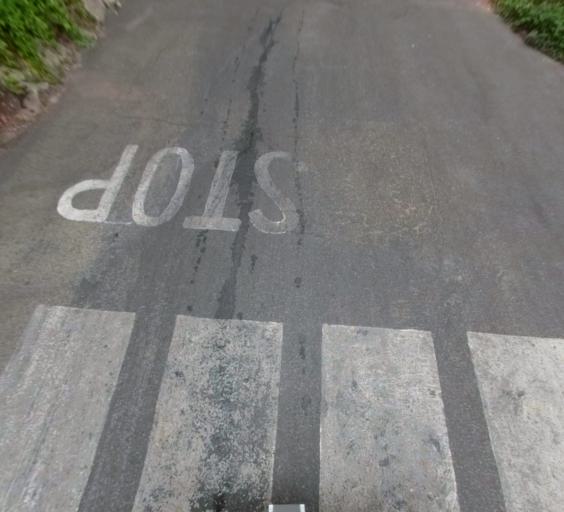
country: US
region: California
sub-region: Madera County
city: Oakhurst
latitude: 37.3197
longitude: -119.5560
